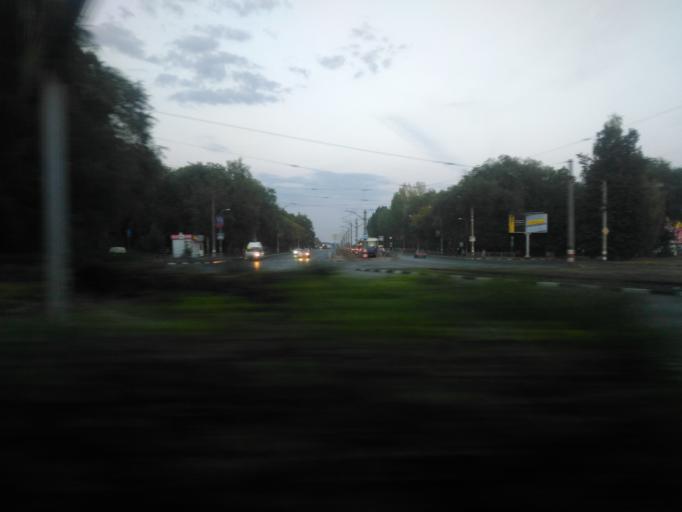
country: RU
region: Ulyanovsk
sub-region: Ulyanovskiy Rayon
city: Ulyanovsk
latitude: 54.2987
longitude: 48.3217
